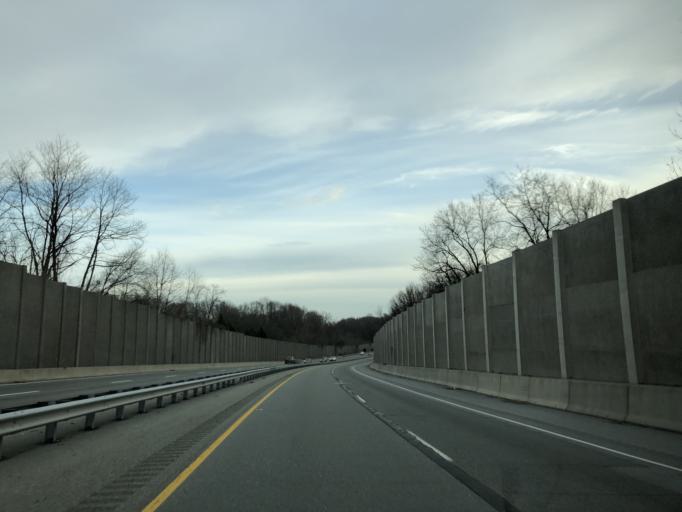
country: US
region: Pennsylvania
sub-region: Chester County
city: Exton
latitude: 40.0027
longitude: -75.5995
